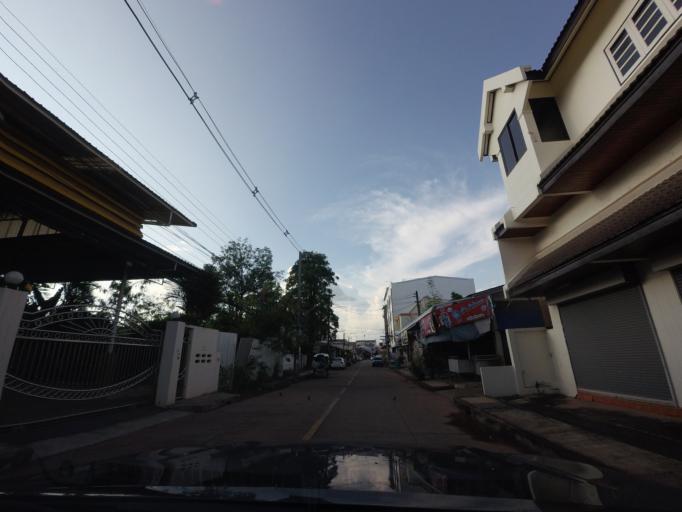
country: TH
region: Nong Khai
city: Nong Khai
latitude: 17.8799
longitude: 102.7479
